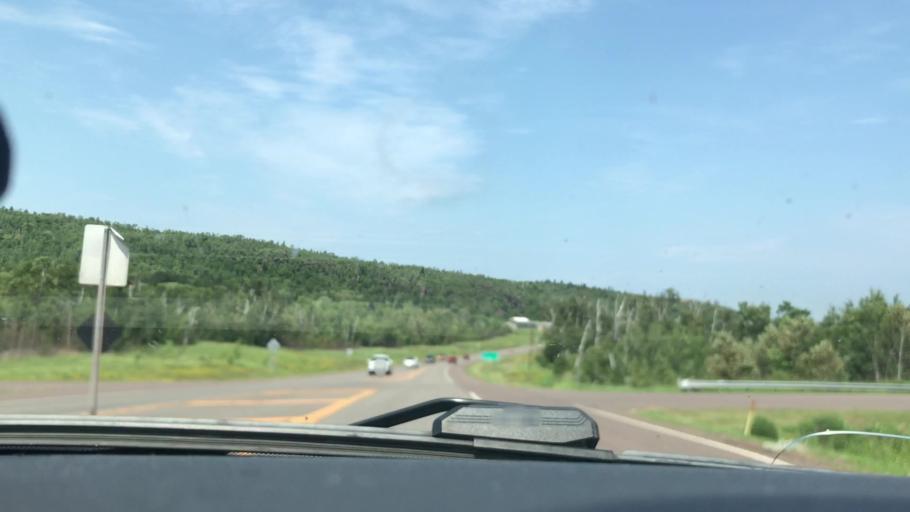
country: US
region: Minnesota
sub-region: Lake County
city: Silver Bay
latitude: 47.2960
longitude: -91.2562
